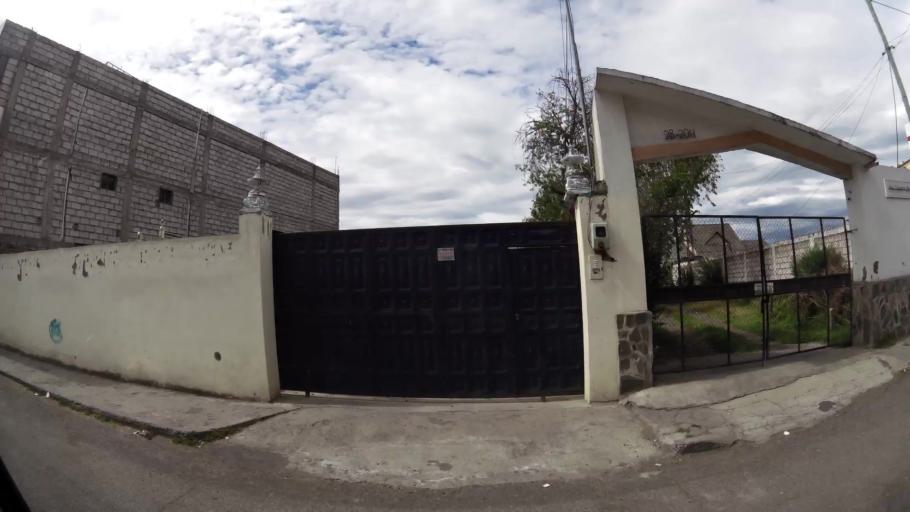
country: EC
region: Cotopaxi
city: Latacunga
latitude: -0.9257
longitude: -78.6063
